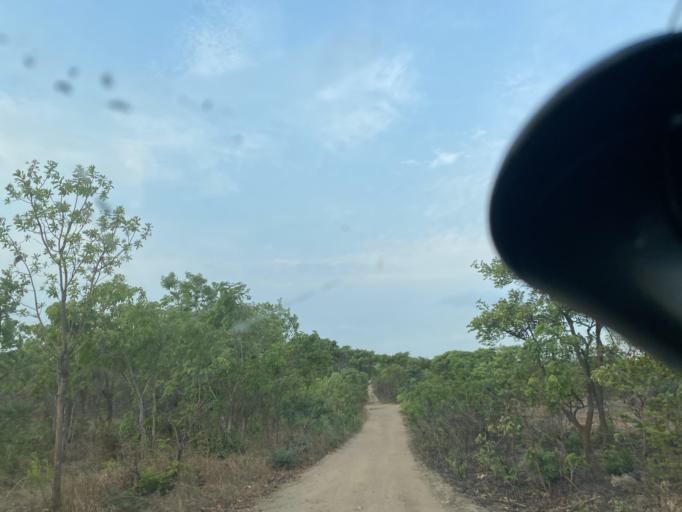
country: ZM
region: Lusaka
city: Chongwe
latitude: -15.2050
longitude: 28.5103
